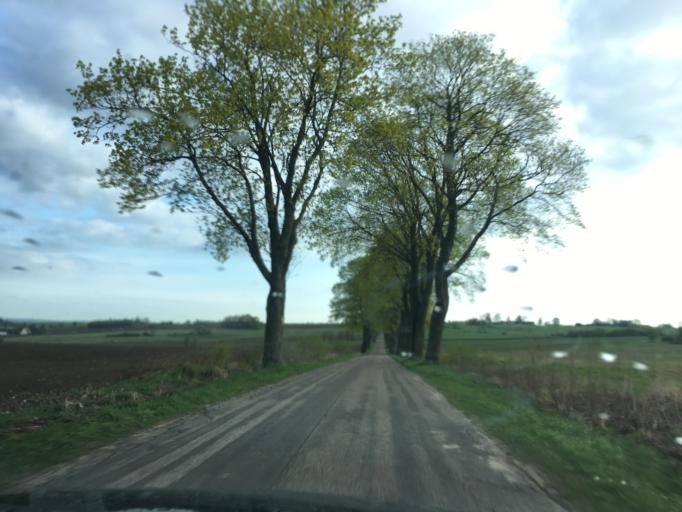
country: PL
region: Warmian-Masurian Voivodeship
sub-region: Powiat ostrodzki
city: Dabrowno
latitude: 53.4297
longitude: 19.9739
